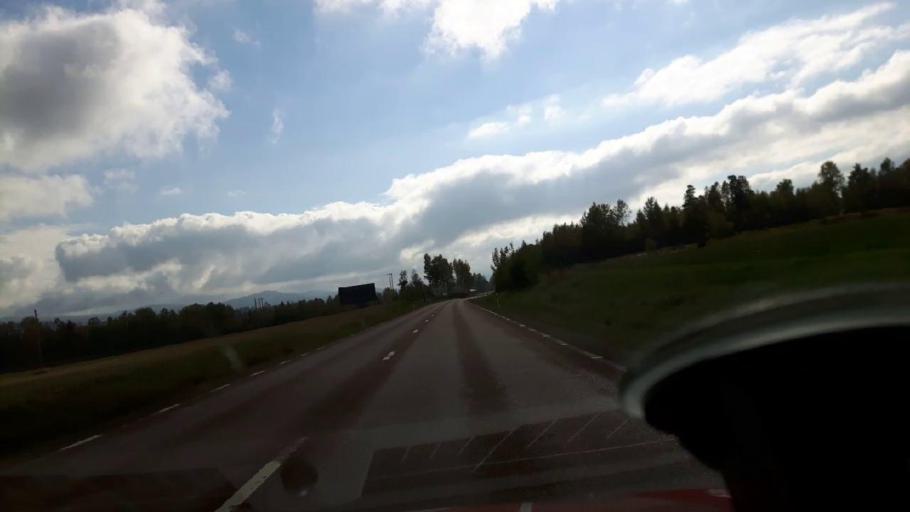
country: SE
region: Gaevleborg
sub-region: Bollnas Kommun
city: Arbra
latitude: 61.5383
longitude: 16.3605
